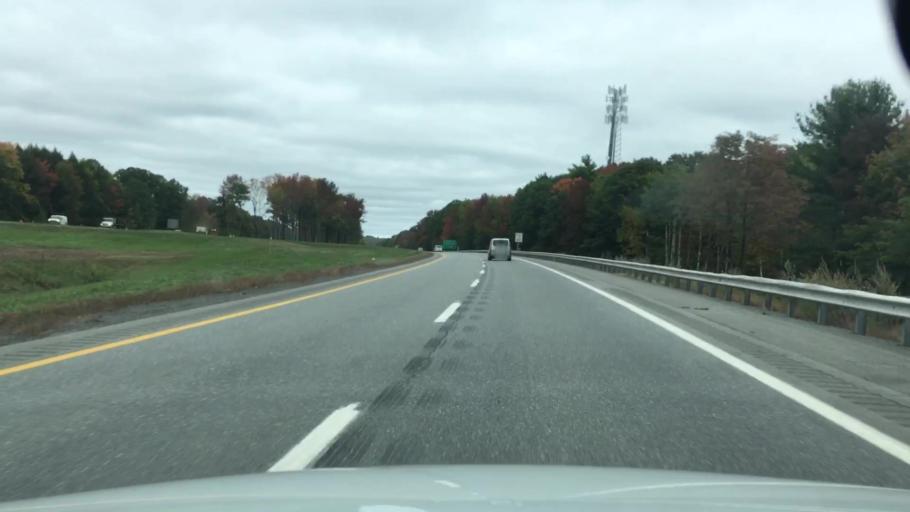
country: US
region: Maine
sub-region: Kennebec County
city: Waterville
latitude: 44.5752
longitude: -69.6314
